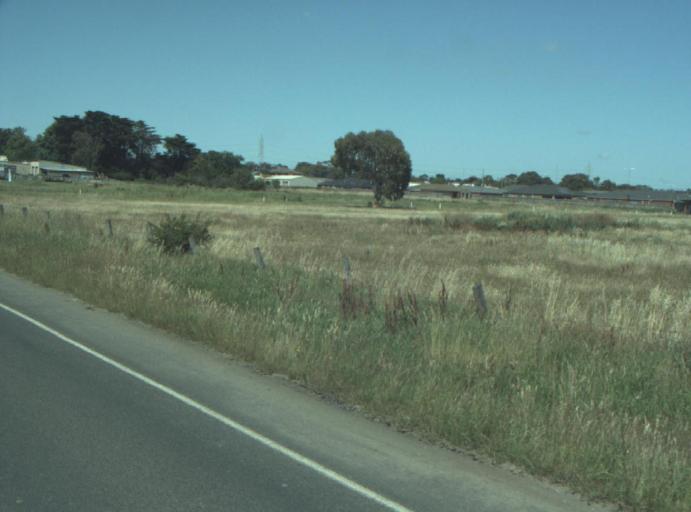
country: AU
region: Victoria
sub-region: Greater Geelong
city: Breakwater
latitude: -38.1937
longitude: 144.3532
